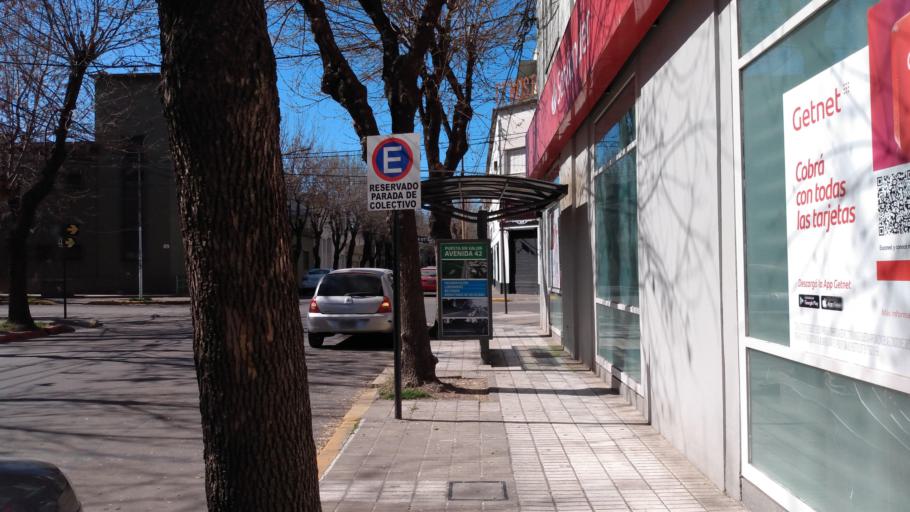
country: AR
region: Buenos Aires
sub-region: Partido de Mercedes
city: Mercedes
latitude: -34.6518
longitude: -59.4315
